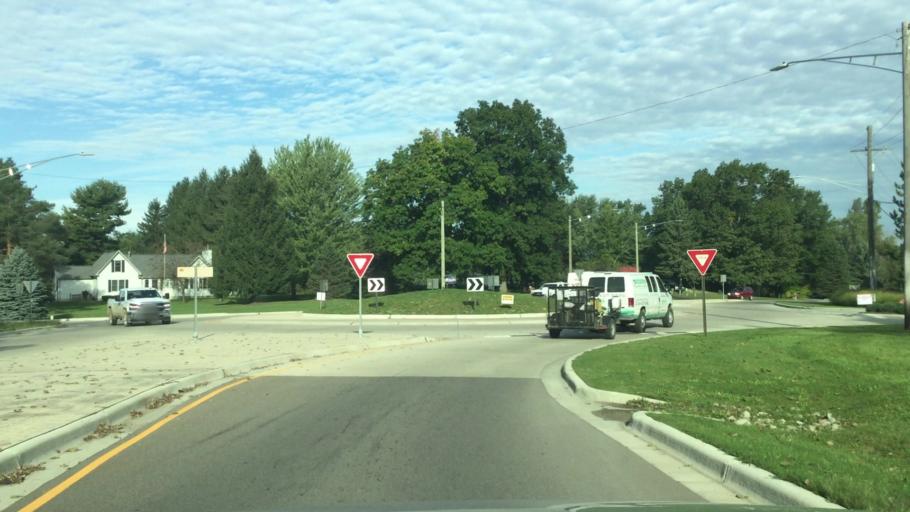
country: US
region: Michigan
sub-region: Livingston County
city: Brighton
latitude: 42.5365
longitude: -83.8709
